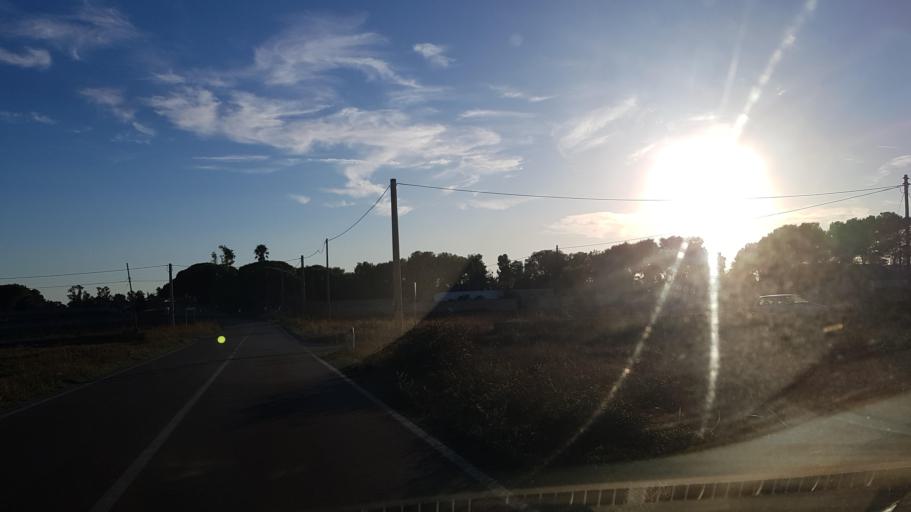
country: IT
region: Apulia
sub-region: Provincia di Lecce
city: Giorgilorio
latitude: 40.4073
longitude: 18.2000
